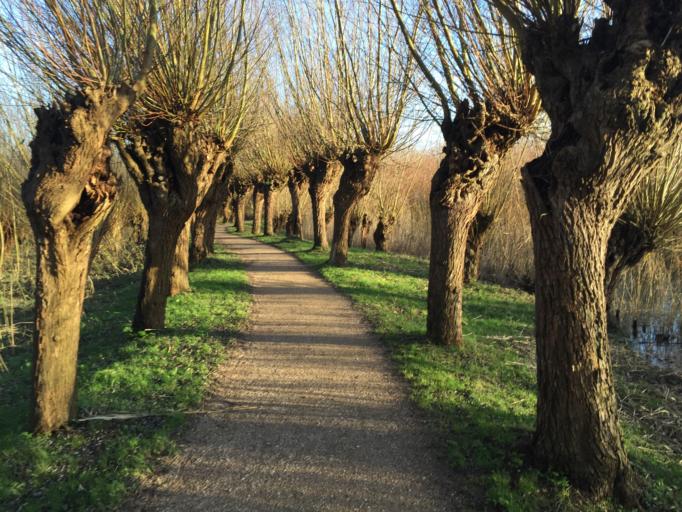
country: NL
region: South Holland
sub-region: Gemeente Albrandswaard
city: Rhoon
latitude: 51.8431
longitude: 4.4300
